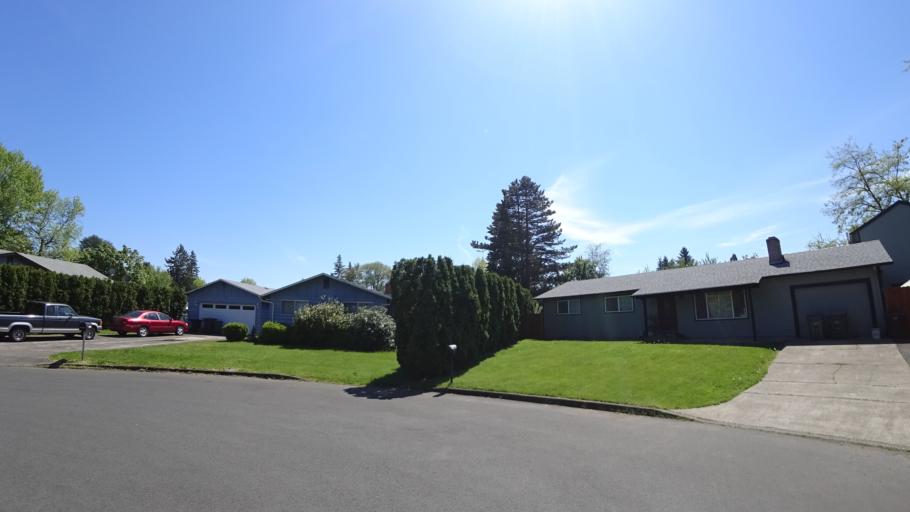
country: US
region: Oregon
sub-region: Washington County
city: Hillsboro
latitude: 45.5124
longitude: -122.9655
